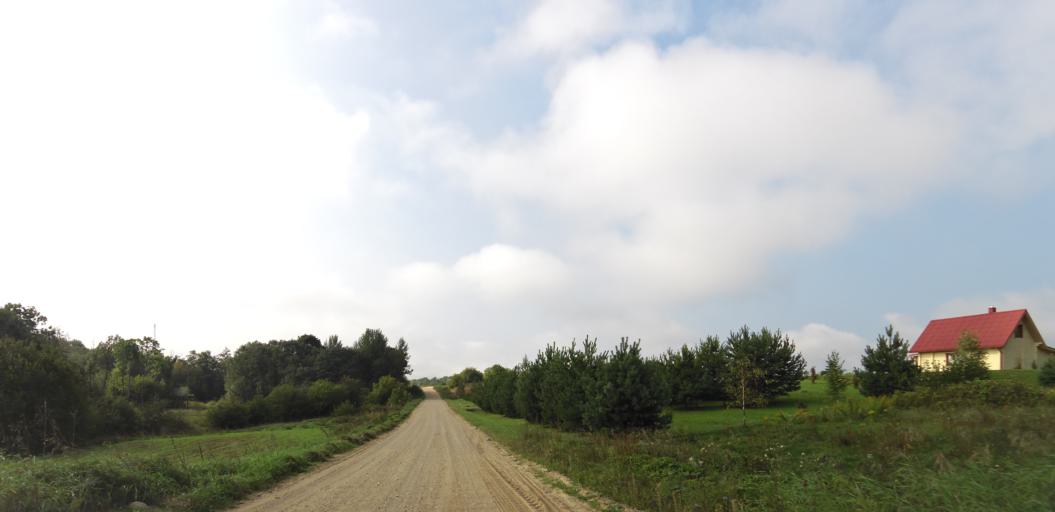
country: LT
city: Grigiskes
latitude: 54.7702
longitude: 25.0544
